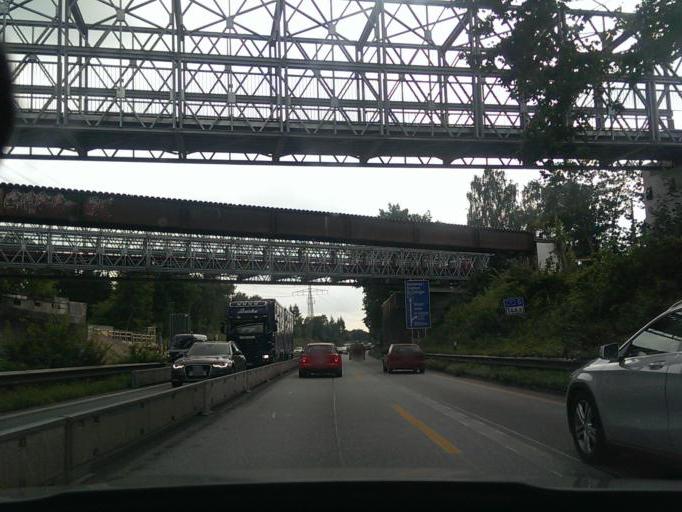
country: DE
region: Hamburg
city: Eidelstedt
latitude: 53.6287
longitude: 9.9217
